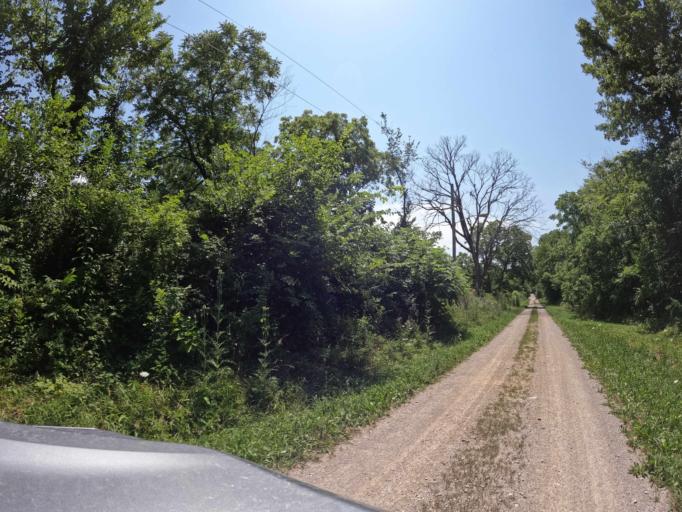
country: US
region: Iowa
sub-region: Appanoose County
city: Centerville
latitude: 40.7806
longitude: -92.9465
